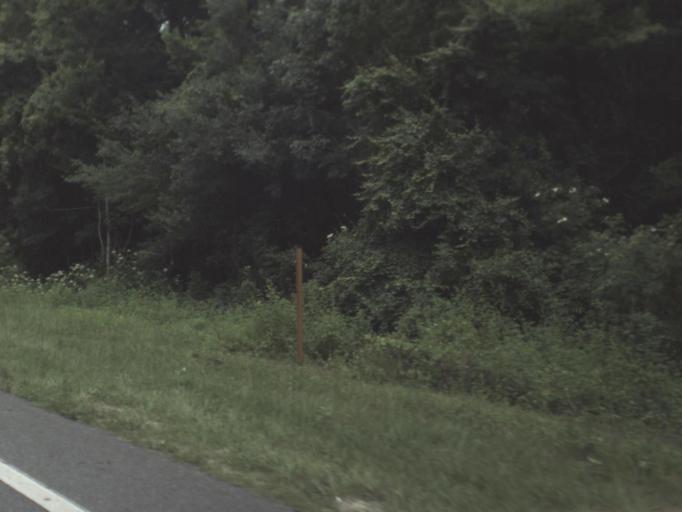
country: US
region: Florida
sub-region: Putnam County
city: Palatka
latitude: 29.5915
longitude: -81.6036
